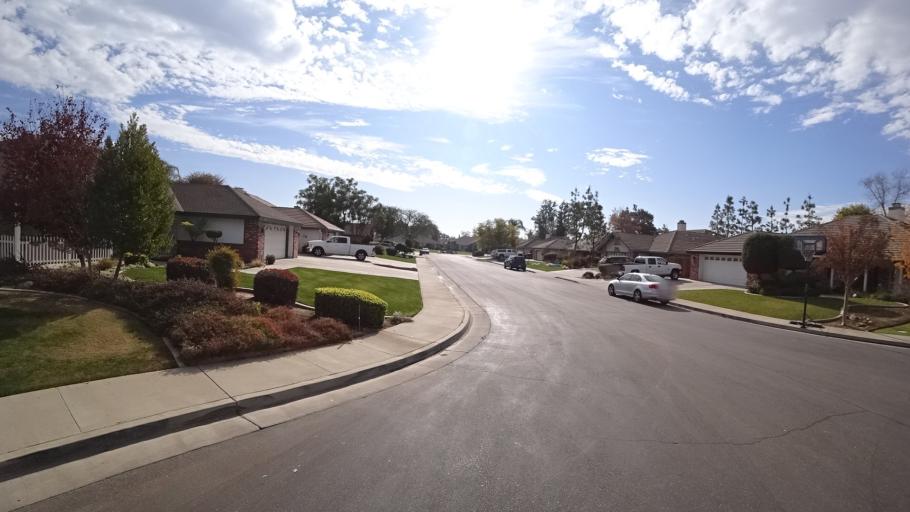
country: US
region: California
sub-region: Kern County
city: Greenacres
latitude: 35.4084
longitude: -119.1260
